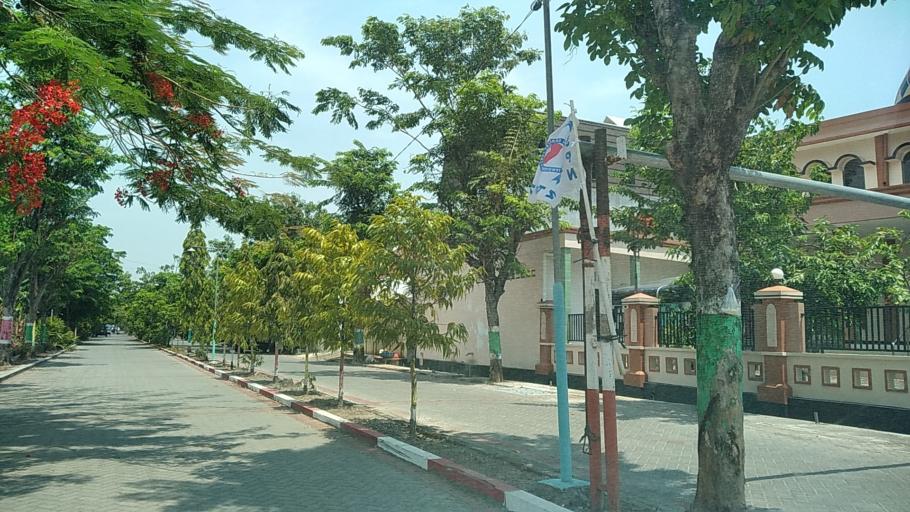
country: ID
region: Central Java
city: Mranggen
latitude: -7.0079
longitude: 110.4846
